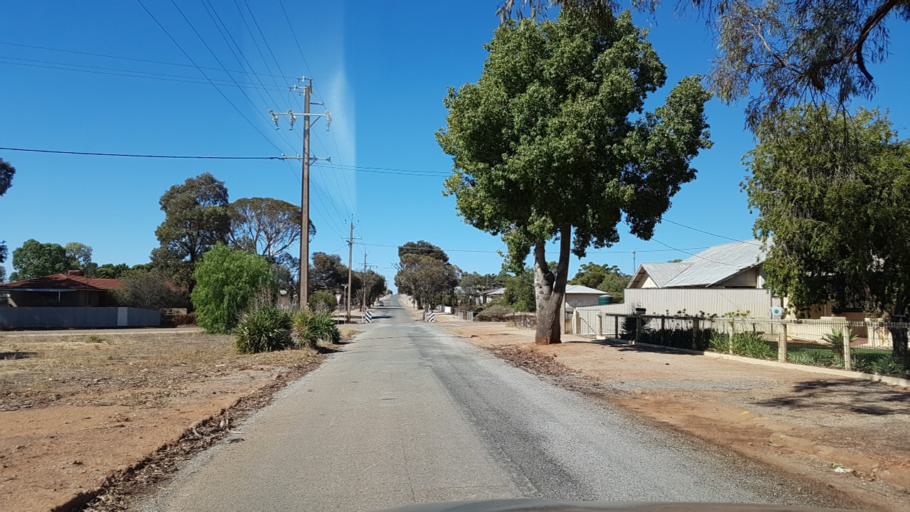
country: AU
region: South Australia
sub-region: Peterborough
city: Peterborough
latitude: -32.9802
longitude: 138.8241
